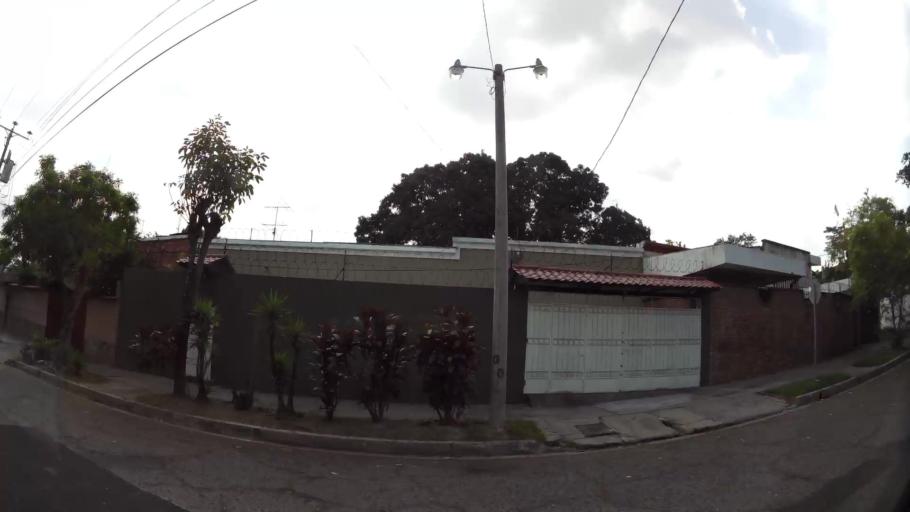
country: SV
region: San Salvador
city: Mejicanos
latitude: 13.7112
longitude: -89.2117
